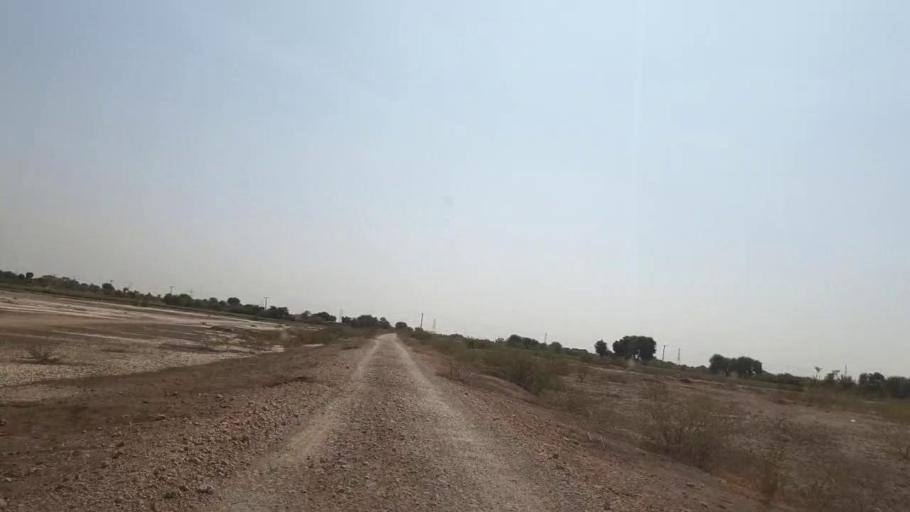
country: PK
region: Sindh
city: Nabisar
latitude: 25.0708
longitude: 69.5527
